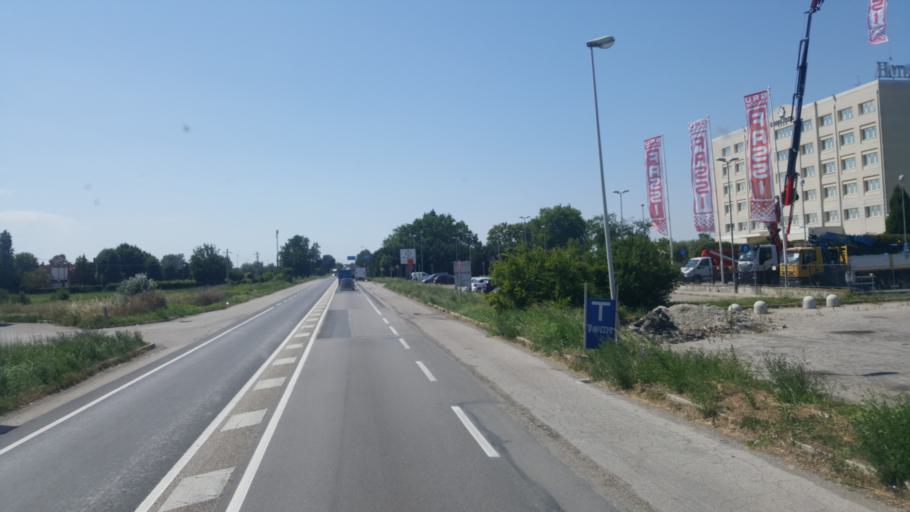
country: IT
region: Emilia-Romagna
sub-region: Provincia di Bologna
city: Castel Maggiore
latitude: 44.5932
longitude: 11.3847
